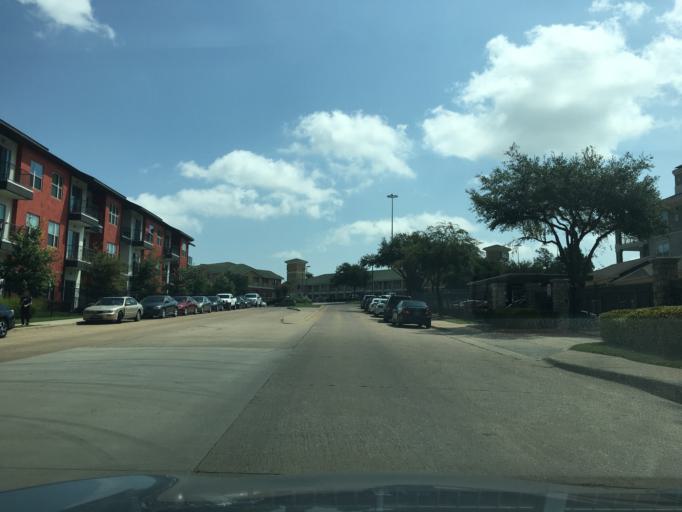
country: US
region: Texas
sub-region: Dallas County
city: Richardson
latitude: 32.9172
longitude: -96.7492
